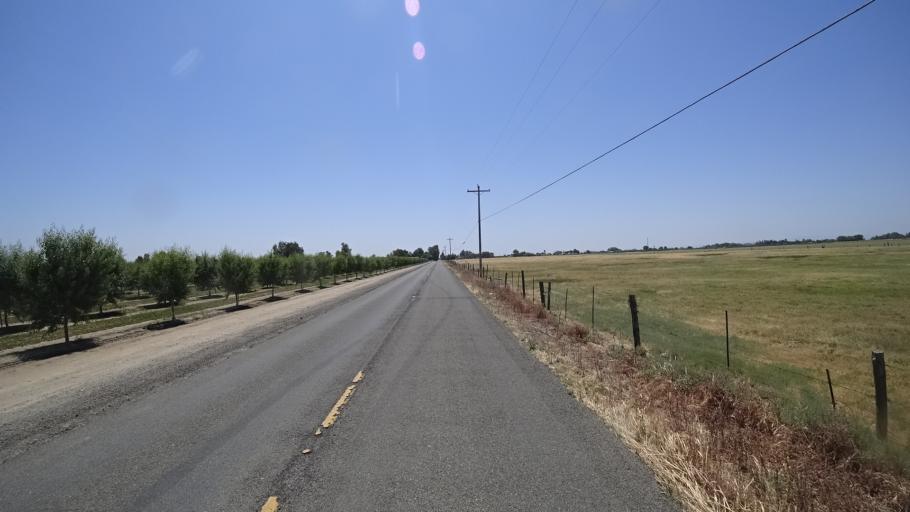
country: US
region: California
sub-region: Kings County
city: Lemoore
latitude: 36.2797
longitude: -119.7629
